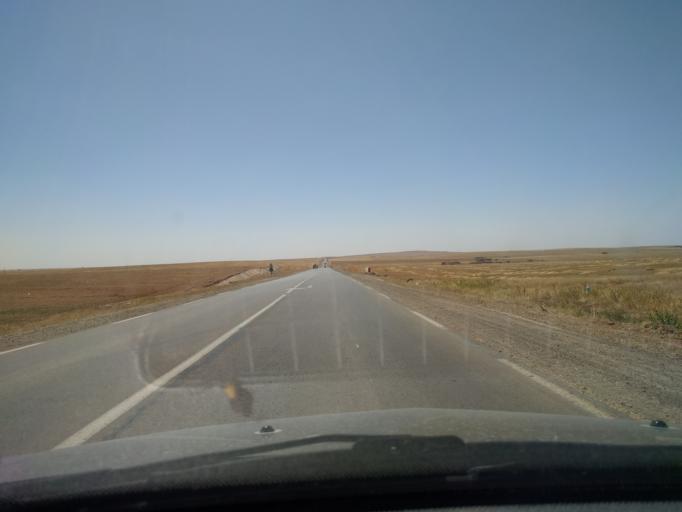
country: DZ
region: Tiaret
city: Frenda
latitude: 34.8911
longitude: 1.1765
